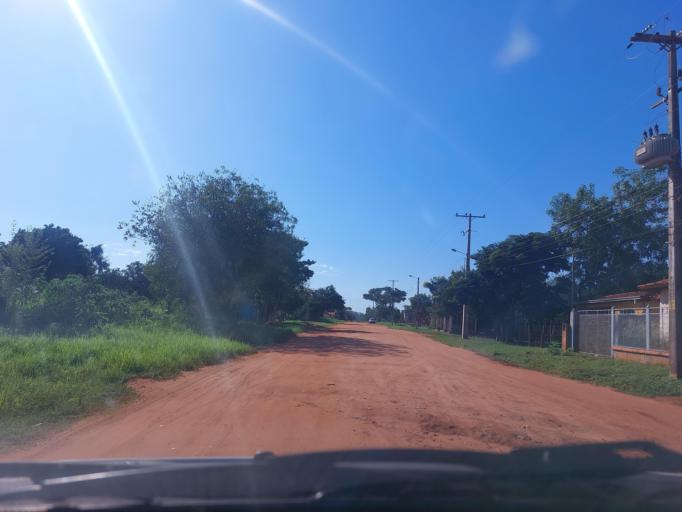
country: PY
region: San Pedro
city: Guayaybi
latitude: -24.5308
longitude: -56.3987
